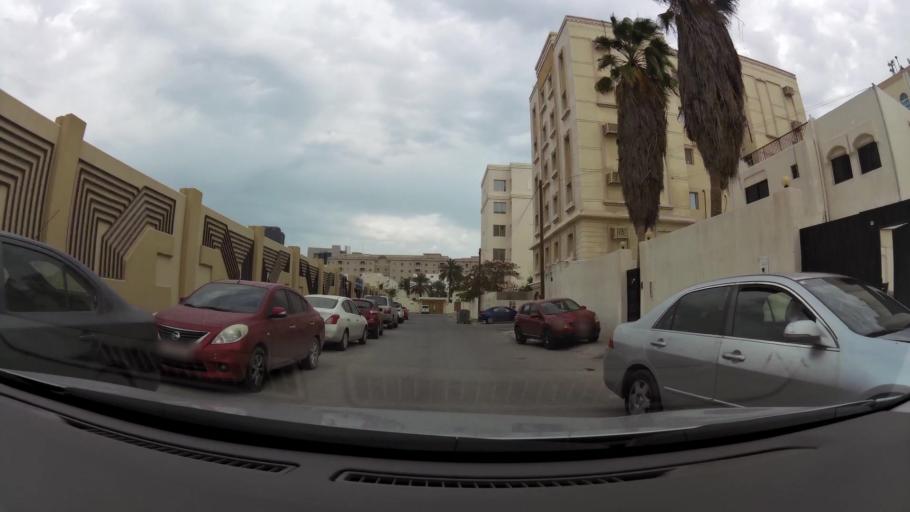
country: QA
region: Baladiyat ad Dawhah
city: Doha
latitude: 25.2780
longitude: 51.5016
